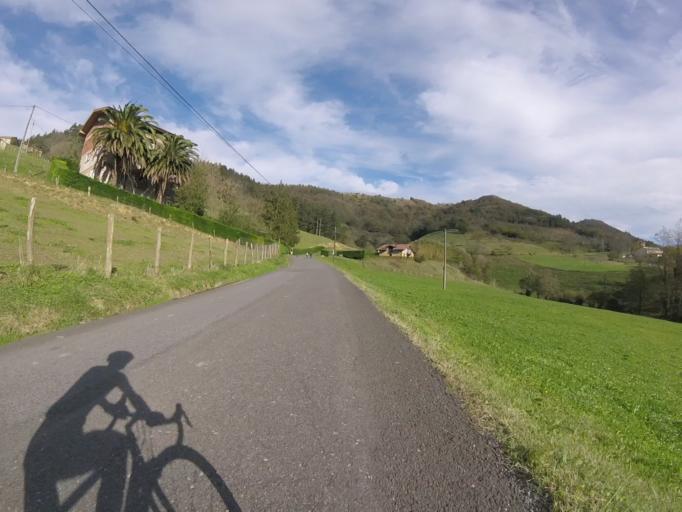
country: ES
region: Basque Country
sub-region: Provincia de Guipuzcoa
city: Orio
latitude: 43.2832
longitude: -2.1112
